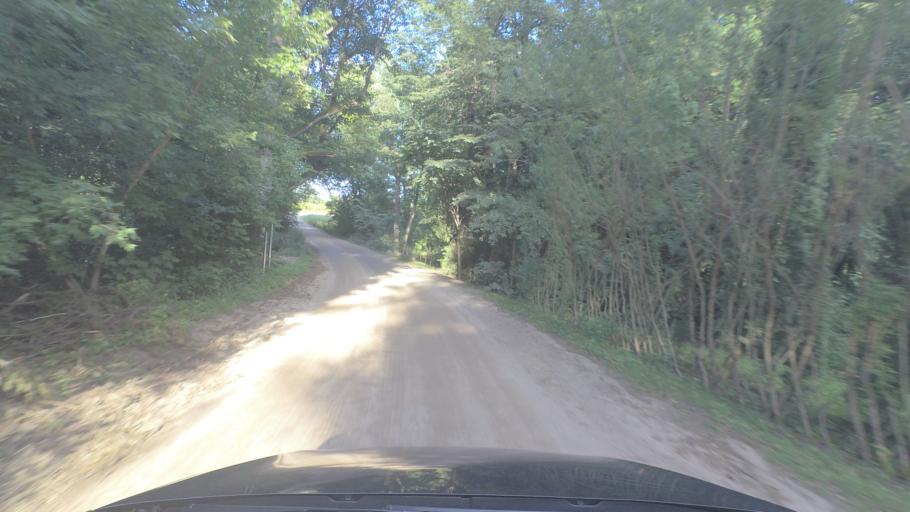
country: LT
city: Svencioneliai
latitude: 55.1665
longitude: 25.8370
